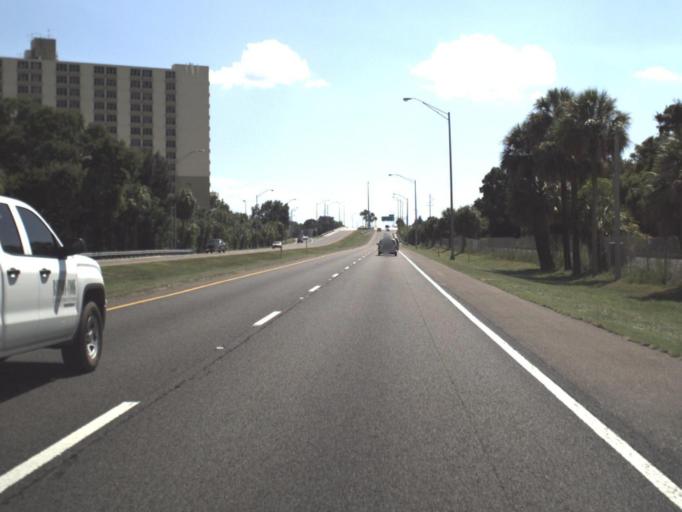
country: US
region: Florida
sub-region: Hillsborough County
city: Tampa
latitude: 27.9241
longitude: -82.4902
